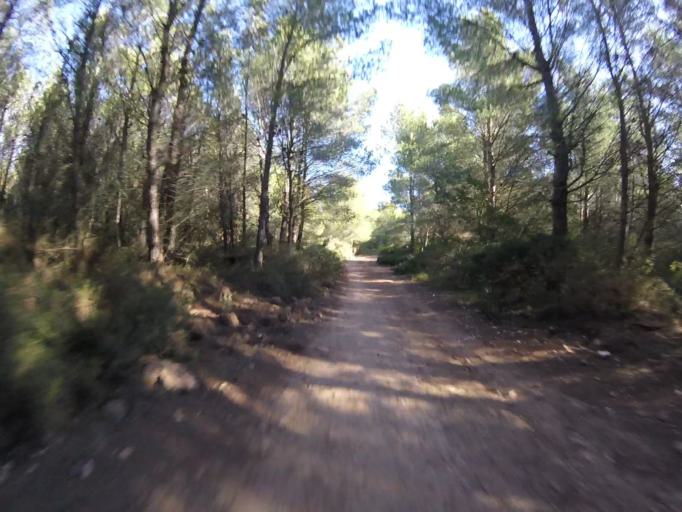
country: ES
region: Valencia
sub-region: Provincia de Castello
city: Benicassim
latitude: 40.0868
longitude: 0.0919
